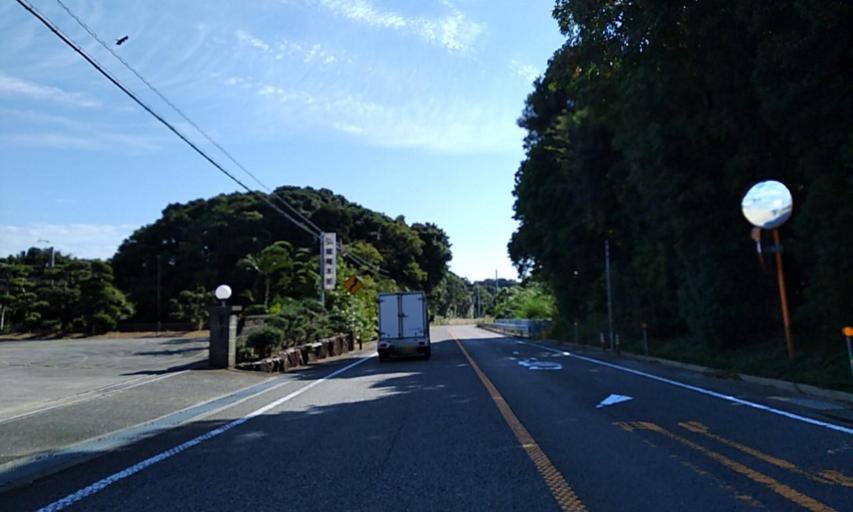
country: JP
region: Wakayama
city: Gobo
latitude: 33.7883
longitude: 135.2345
